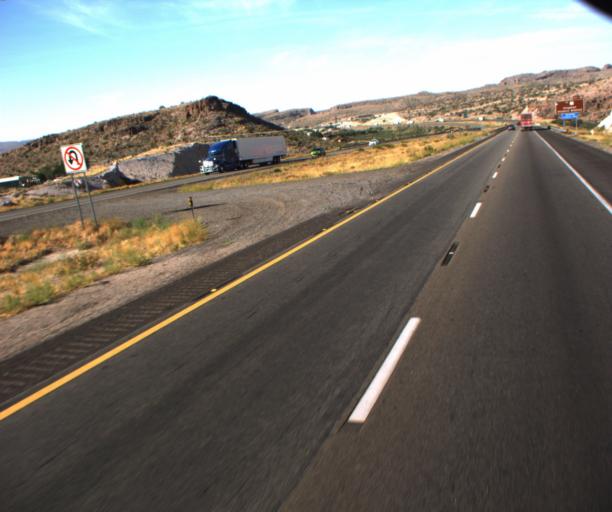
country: US
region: Arizona
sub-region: Mohave County
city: Kingman
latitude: 35.2055
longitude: -114.0619
